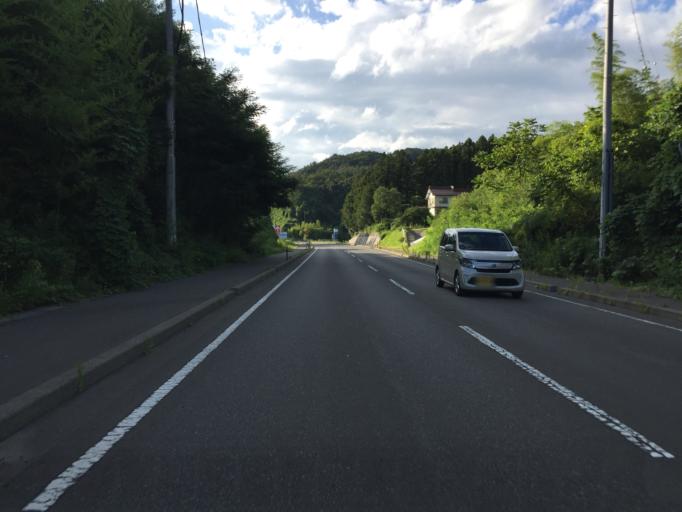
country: JP
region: Fukushima
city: Fukushima-shi
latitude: 37.7202
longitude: 140.4988
